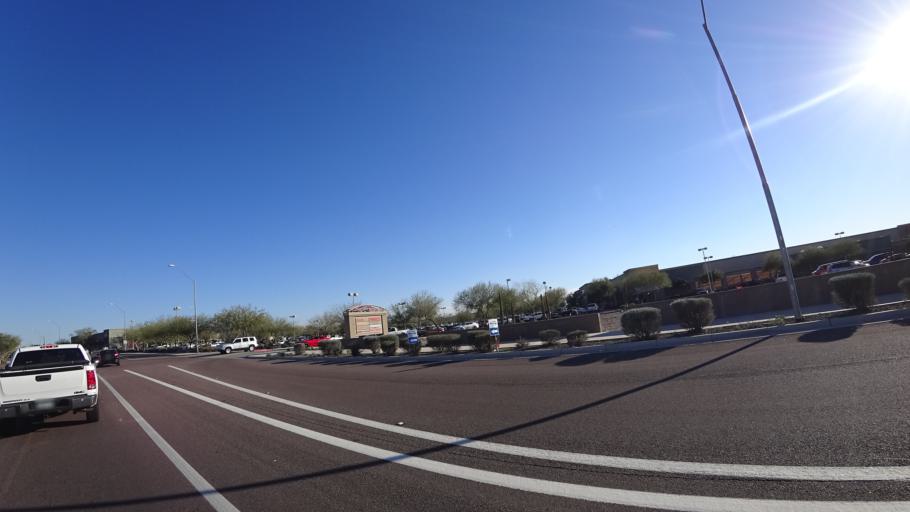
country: US
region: Arizona
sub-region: Maricopa County
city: Sun City West
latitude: 33.7114
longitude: -112.2752
